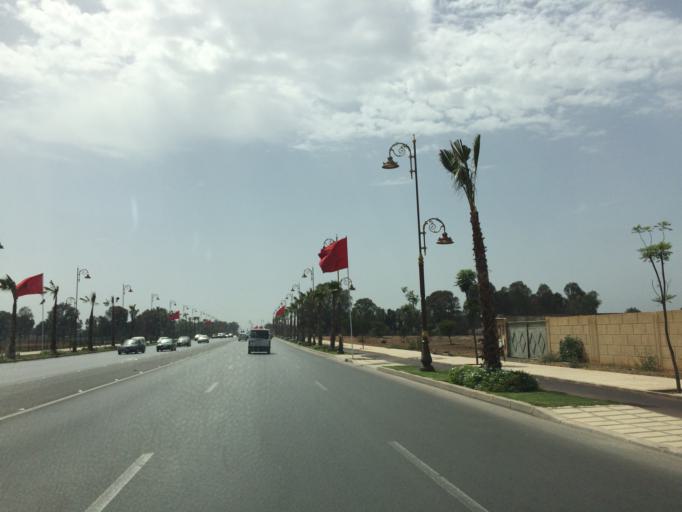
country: MA
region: Rabat-Sale-Zemmour-Zaer
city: Sale
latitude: 34.0327
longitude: -6.7711
